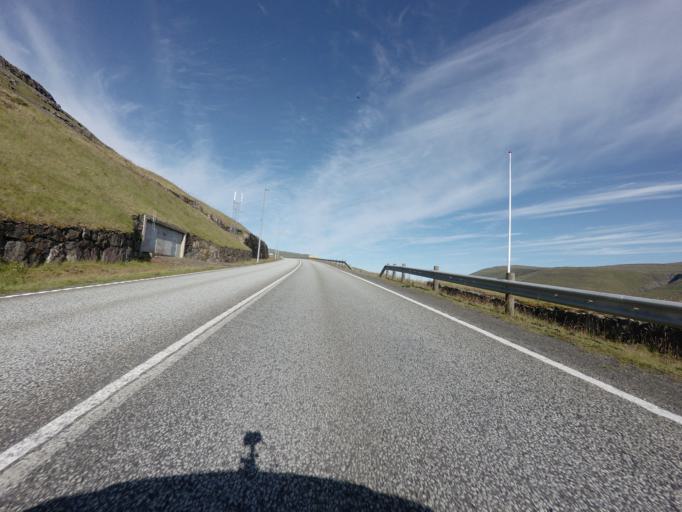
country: FO
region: Streymoy
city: Vestmanna
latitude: 62.0992
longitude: -7.1171
